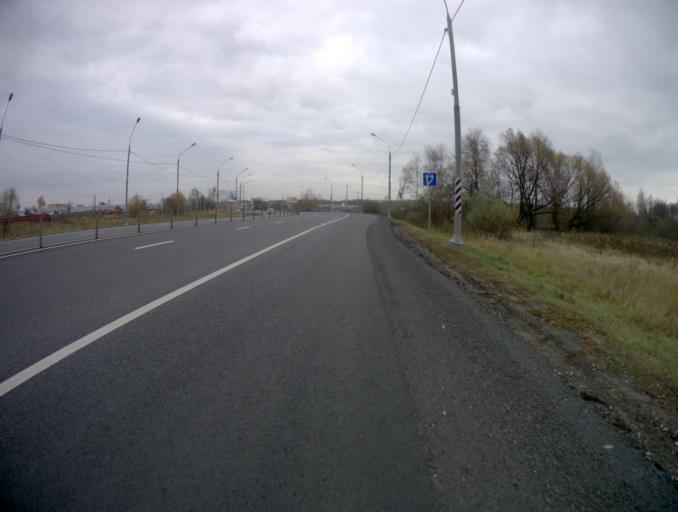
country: RU
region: Moskovskaya
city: Malaya Dubna
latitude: 55.8734
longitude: 38.9635
